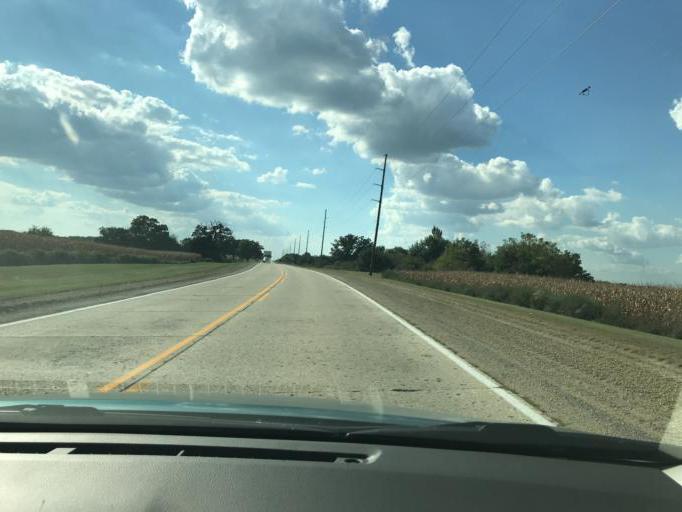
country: US
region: Wisconsin
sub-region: Rock County
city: Orfordville
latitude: 42.5571
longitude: -89.2892
